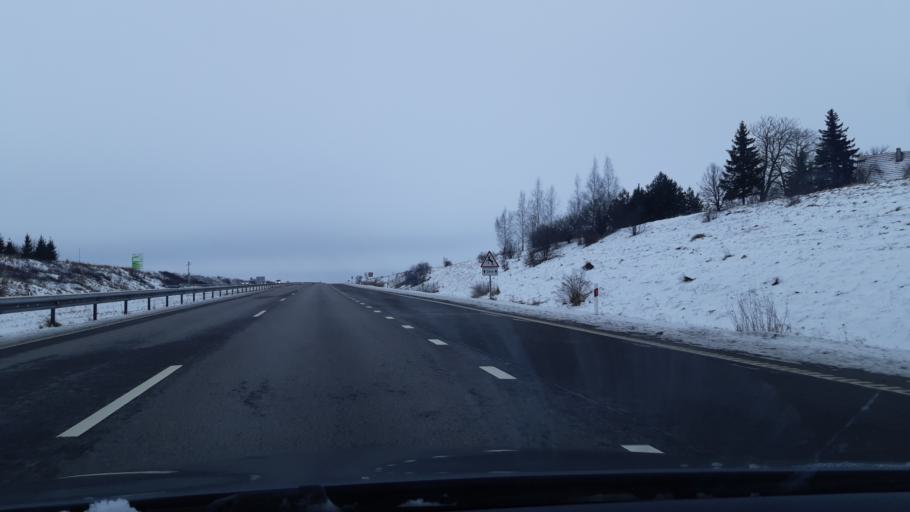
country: LT
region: Kauno apskritis
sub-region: Kaunas
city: Sargenai
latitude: 55.1095
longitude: 23.7760
